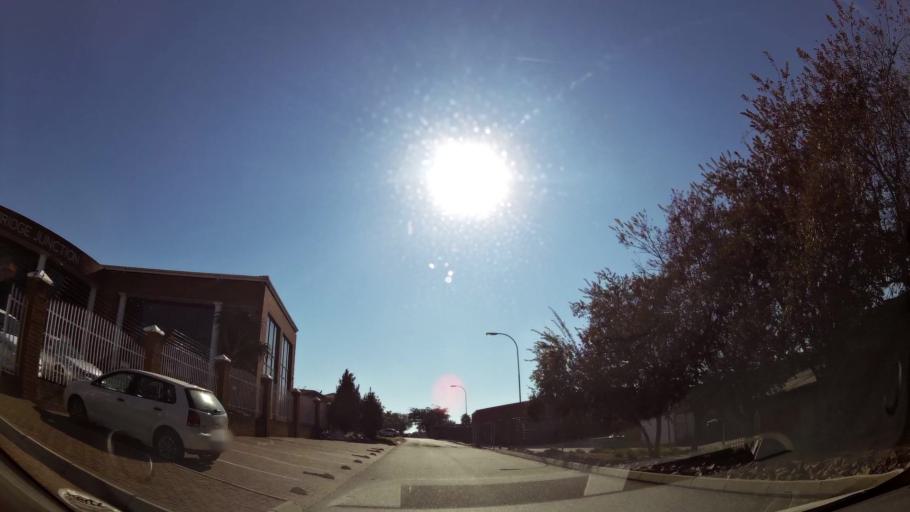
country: ZA
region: Mpumalanga
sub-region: Nkangala District Municipality
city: Witbank
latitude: -25.8764
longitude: 29.2456
